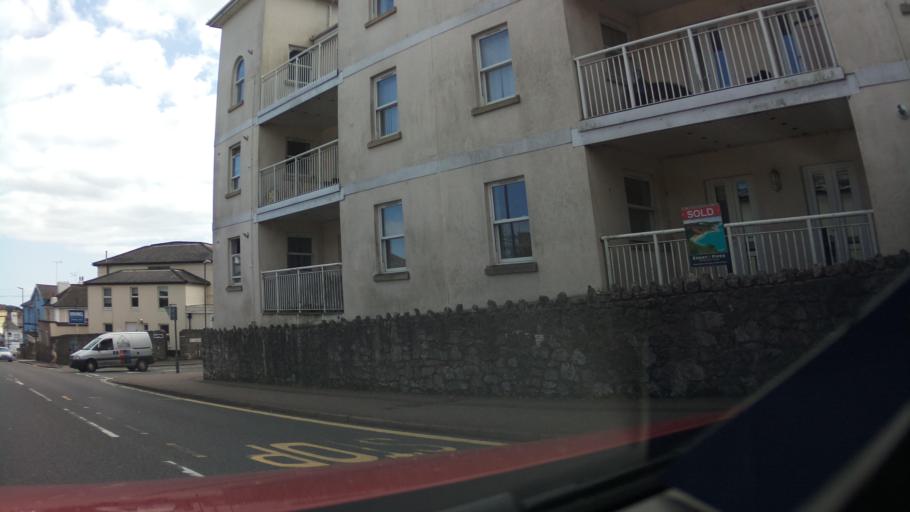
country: GB
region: England
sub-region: Borough of Torbay
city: Torquay
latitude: 50.4799
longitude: -3.5177
